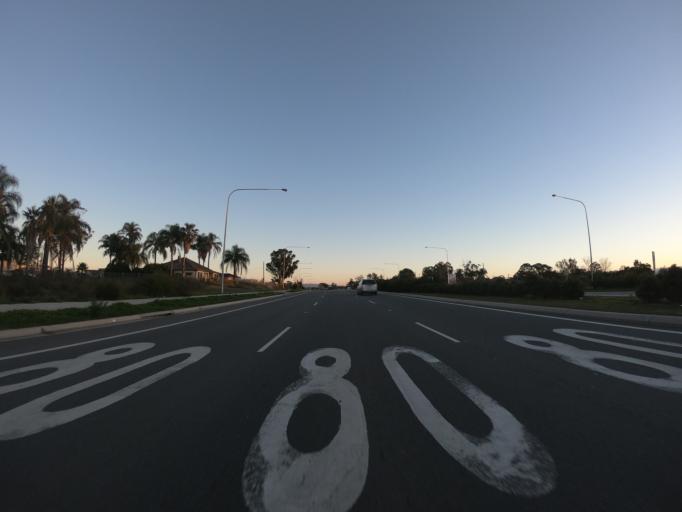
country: AU
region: New South Wales
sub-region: Blacktown
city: Hassall Grove
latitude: -33.7058
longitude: 150.8382
